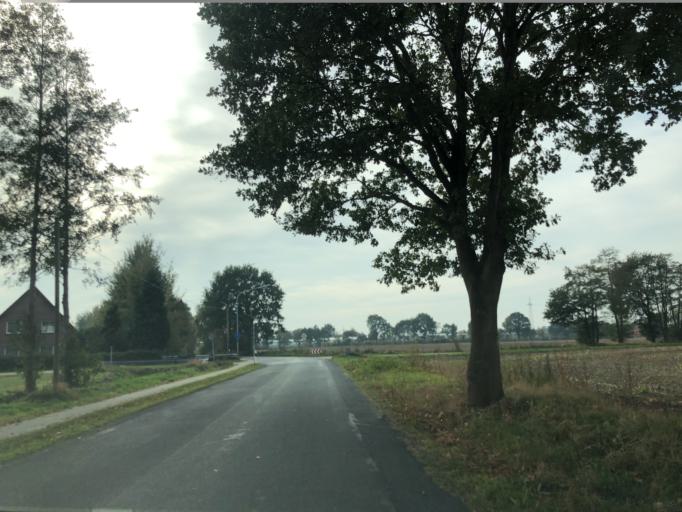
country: DE
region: Lower Saxony
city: Papenburg
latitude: 53.0602
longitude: 7.3912
